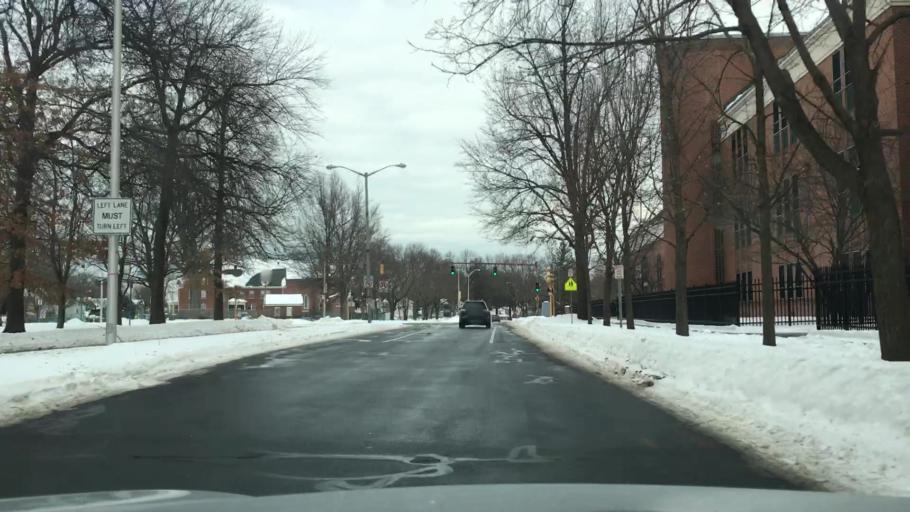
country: US
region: Massachusetts
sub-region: Hampden County
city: West Springfield
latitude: 42.1175
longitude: -72.6135
